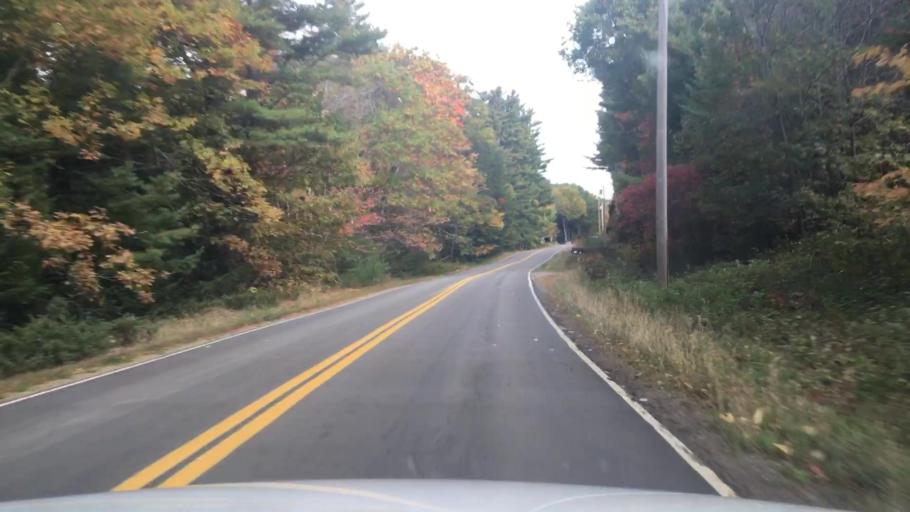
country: US
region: Maine
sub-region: Waldo County
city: Searsmont
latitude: 44.4216
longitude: -69.1419
